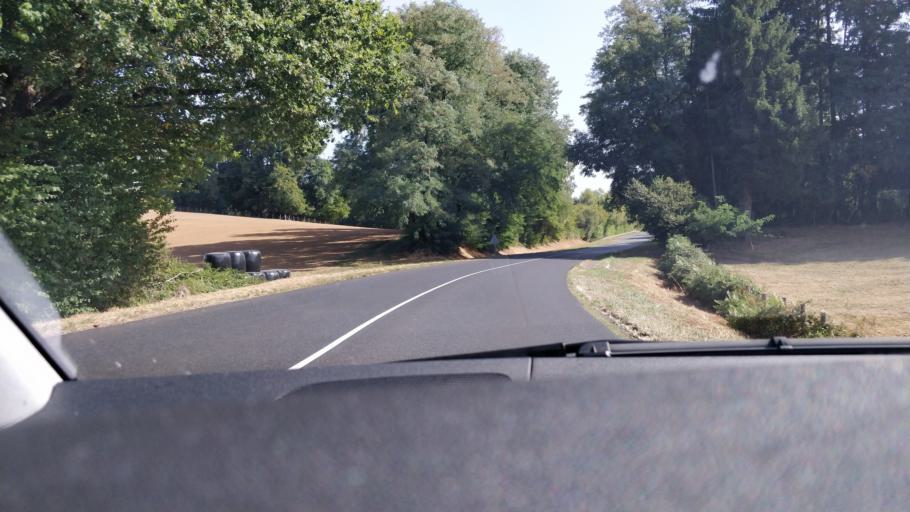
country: FR
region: Limousin
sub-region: Departement de la Correze
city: Uzerche
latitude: 45.4649
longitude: 1.5520
